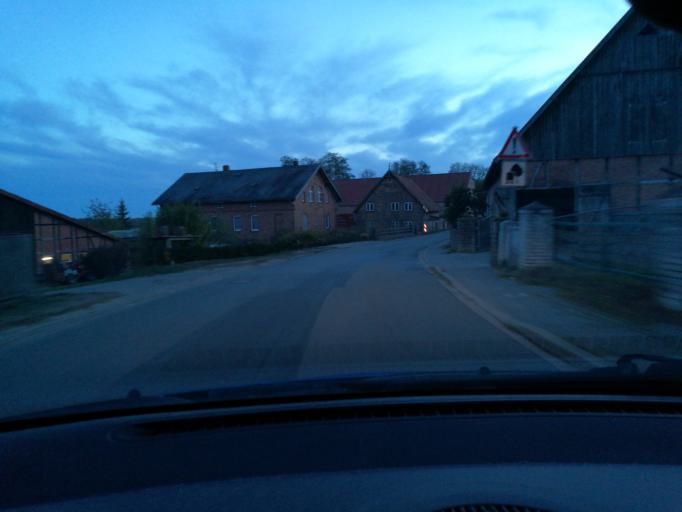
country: DE
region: Lower Saxony
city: Gartow
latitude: 53.0601
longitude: 11.4564
